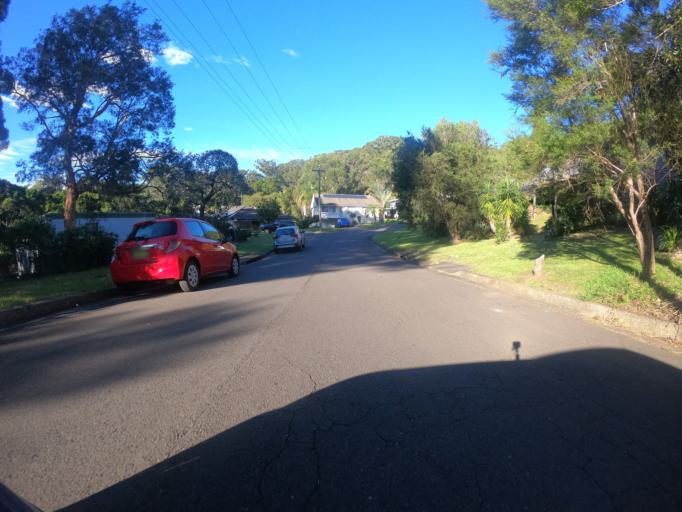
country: AU
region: New South Wales
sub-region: Wollongong
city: Bulli
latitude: -34.3249
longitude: 150.9041
